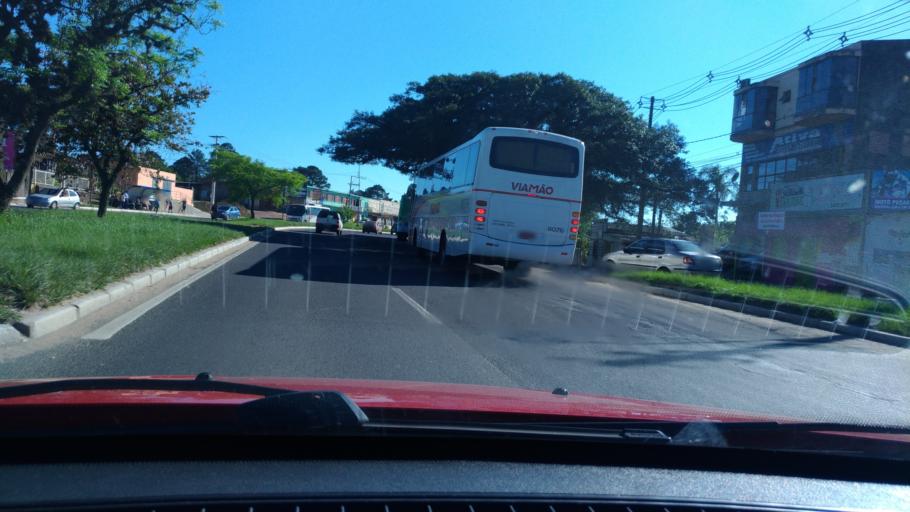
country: BR
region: Rio Grande do Sul
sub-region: Viamao
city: Viamao
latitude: -30.0911
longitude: -51.0631
